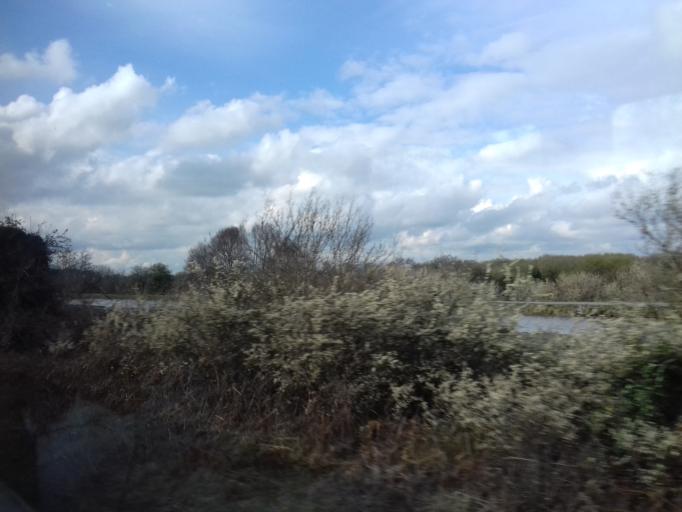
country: IE
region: Leinster
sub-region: An Mhi
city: Ballivor
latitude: 53.4703
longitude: -6.9867
